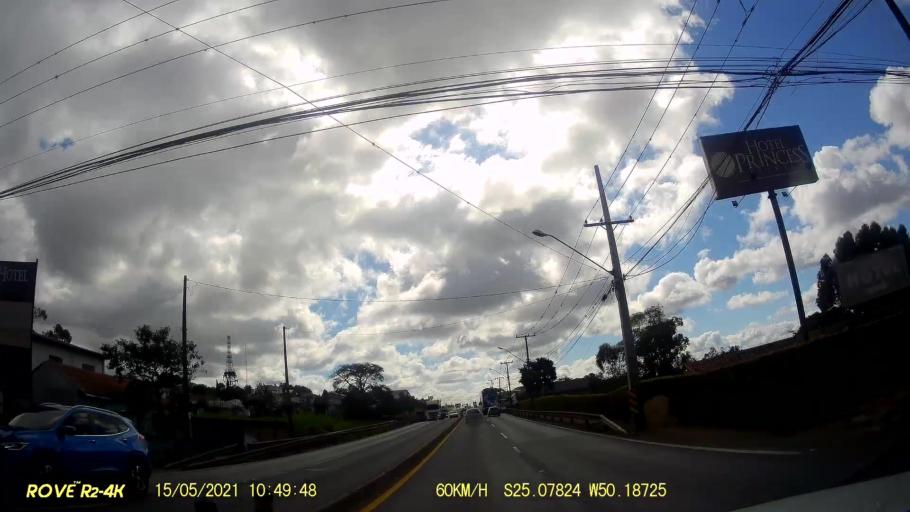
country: BR
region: Parana
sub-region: Ponta Grossa
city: Ponta Grossa
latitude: -25.0780
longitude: -50.1873
